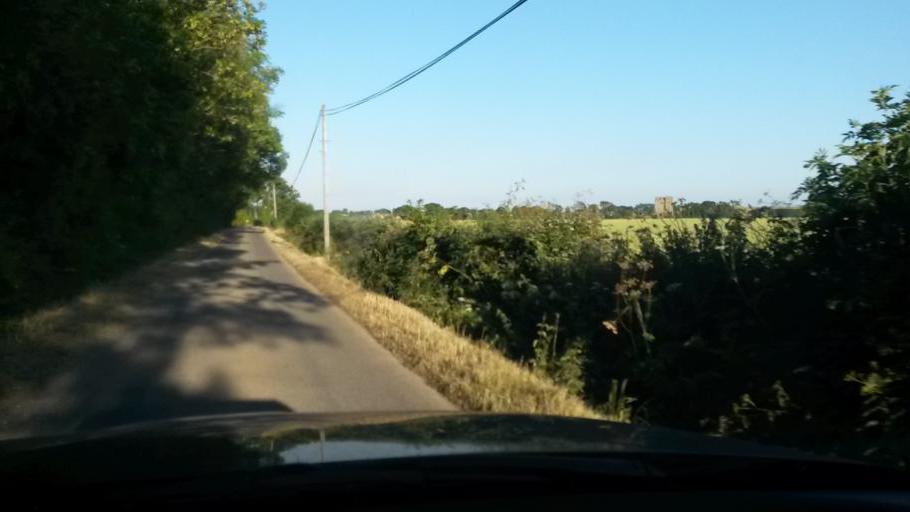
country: IE
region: Leinster
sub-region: Dublin City
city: Finglas
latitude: 53.4319
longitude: -6.3244
